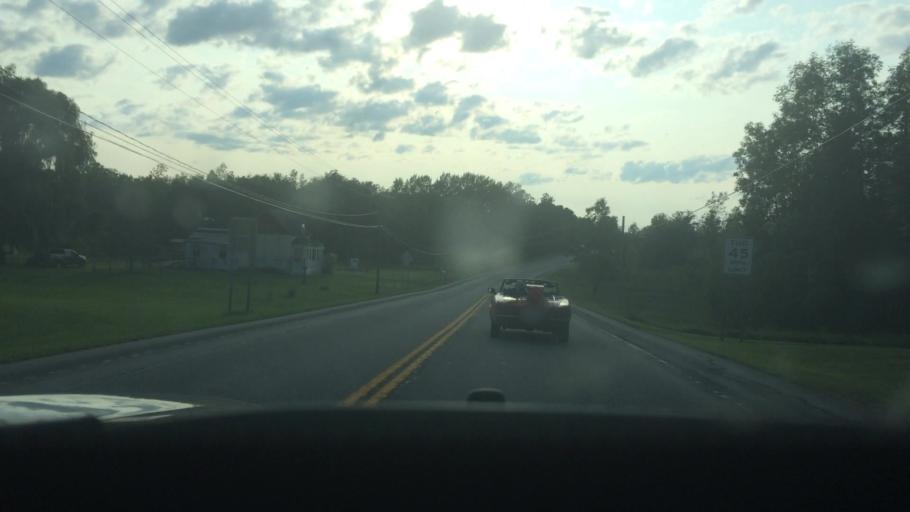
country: US
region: New York
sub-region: St. Lawrence County
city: Ogdensburg
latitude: 44.6659
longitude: -75.3628
